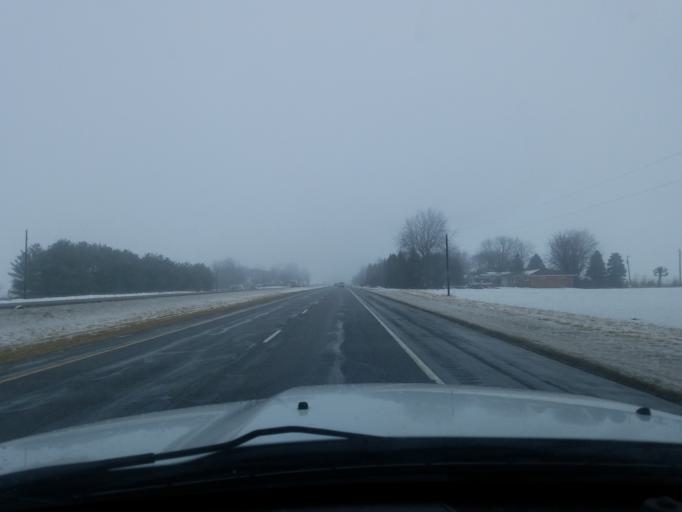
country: US
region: Indiana
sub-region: Tipton County
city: Tipton
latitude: 40.3056
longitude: -86.1268
